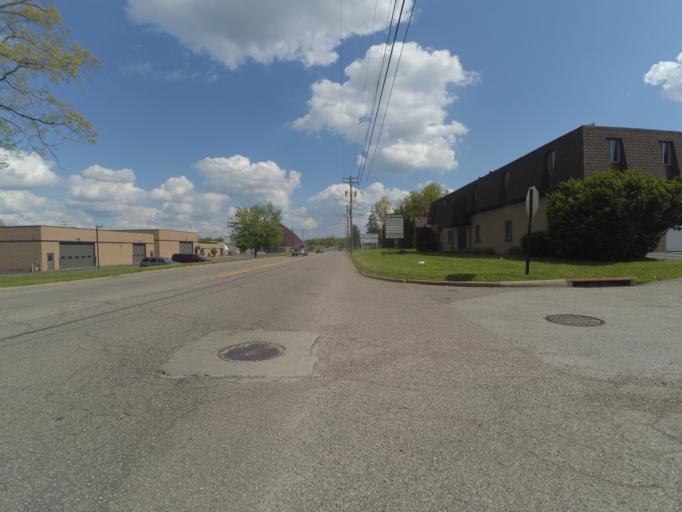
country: US
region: Ohio
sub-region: Mahoning County
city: Austintown
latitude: 41.0929
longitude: -80.7088
